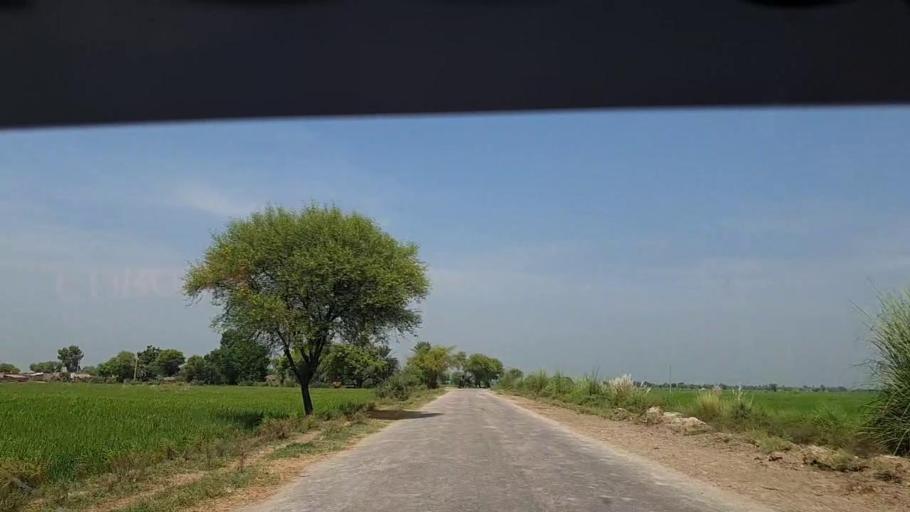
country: PK
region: Sindh
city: Thul
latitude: 28.1353
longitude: 68.7171
